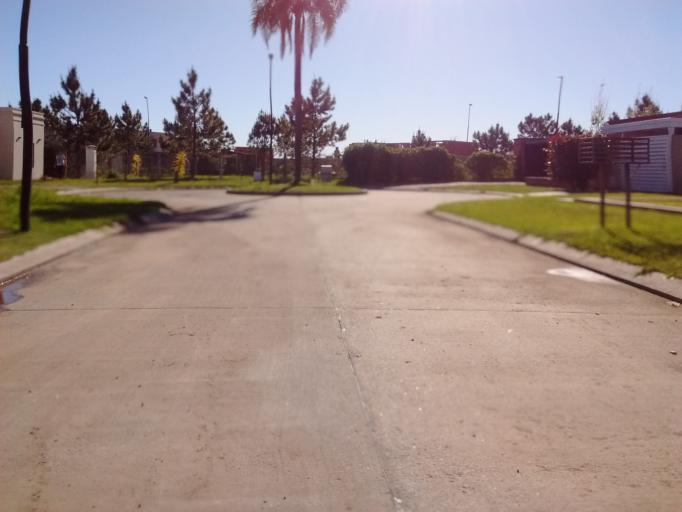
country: AR
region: Santa Fe
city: Funes
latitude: -32.9252
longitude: -60.8478
